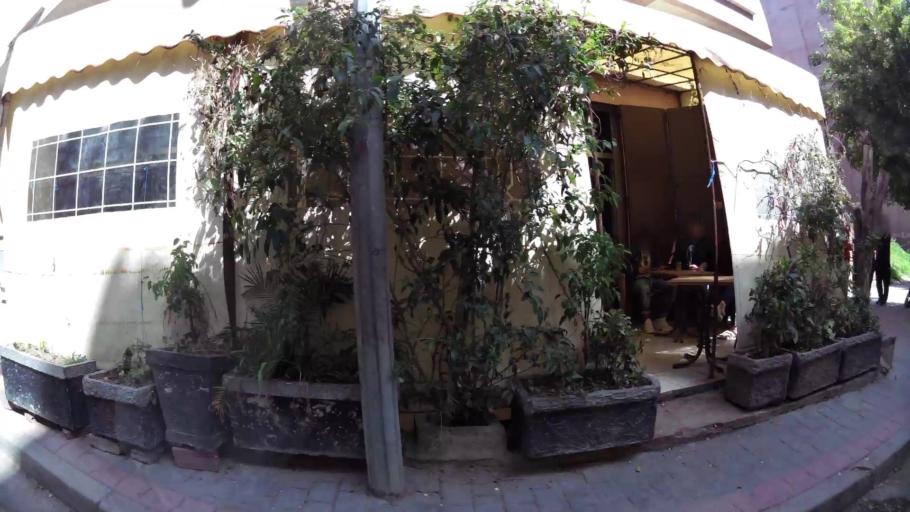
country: MA
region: Tanger-Tetouan
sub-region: Tanger-Assilah
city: Tangier
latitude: 35.7372
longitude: -5.8075
